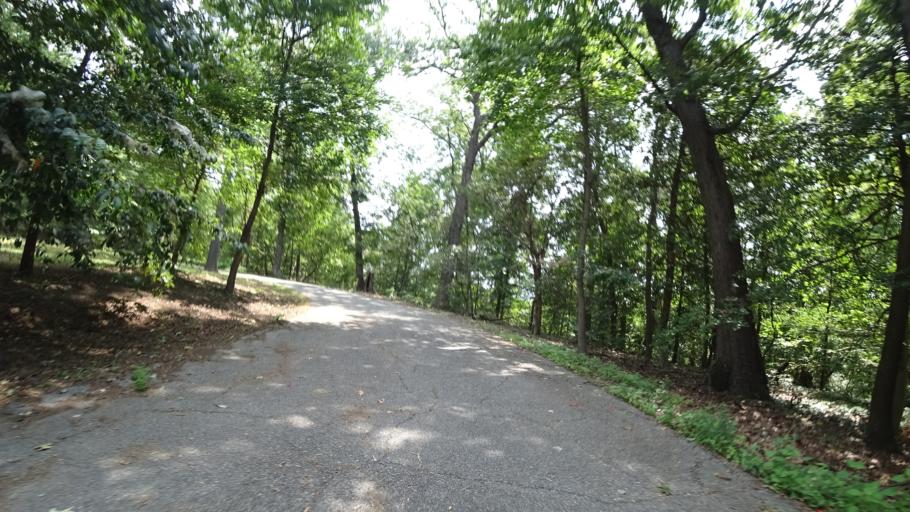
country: US
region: Maryland
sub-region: Prince George's County
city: Colmar Manor
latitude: 38.9097
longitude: -76.9581
